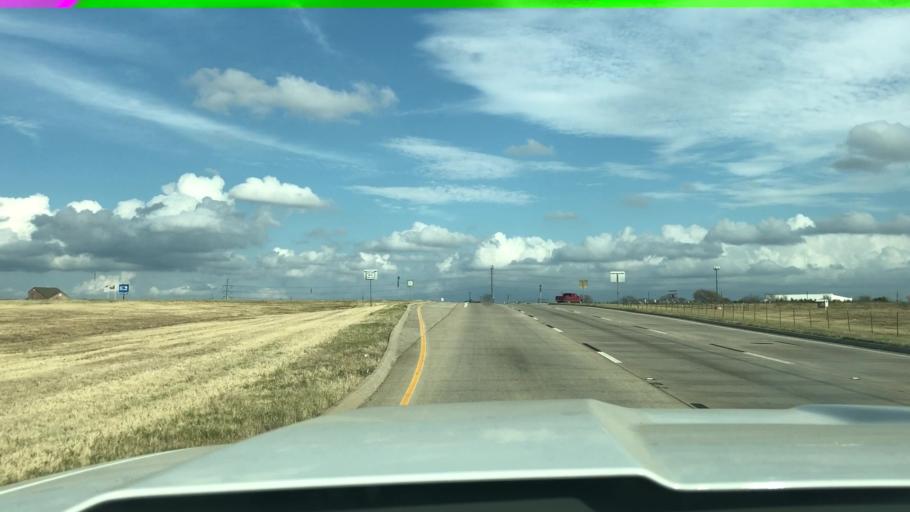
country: US
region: Texas
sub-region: Tarrant County
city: Keller
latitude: 32.9742
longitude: -97.2723
